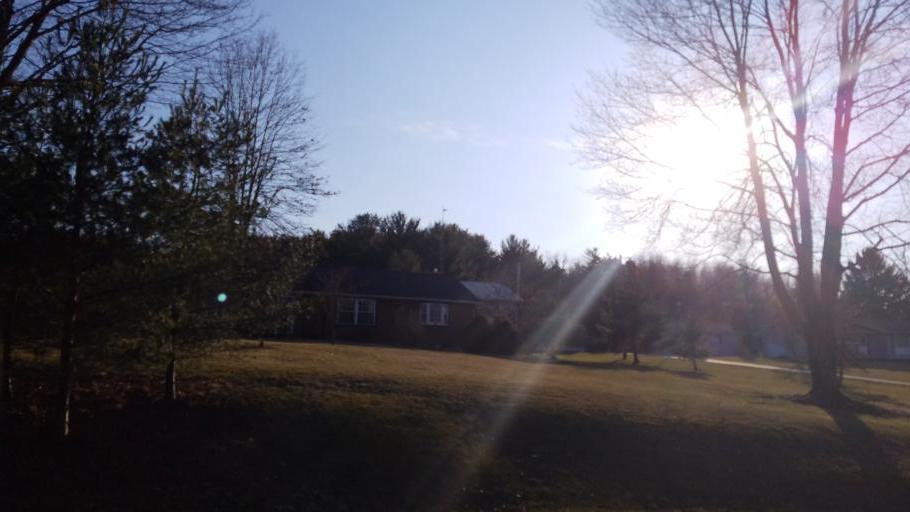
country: US
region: Ohio
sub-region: Richland County
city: Lexington
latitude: 40.7061
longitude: -82.6430
